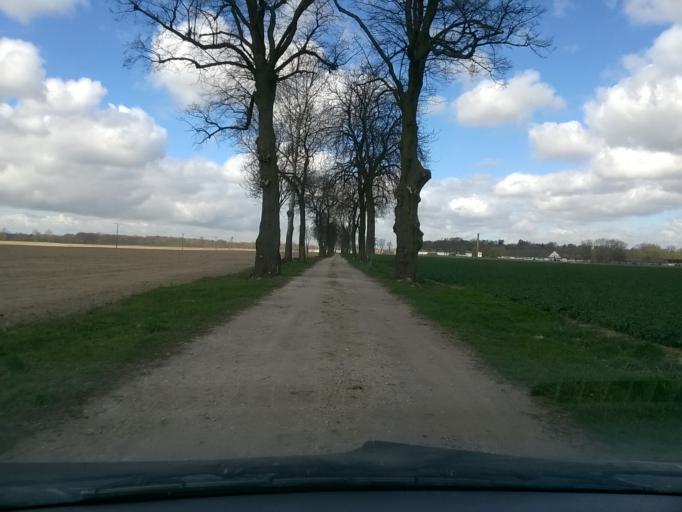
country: PL
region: Kujawsko-Pomorskie
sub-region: Powiat nakielski
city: Kcynia
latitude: 52.9842
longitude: 17.4342
